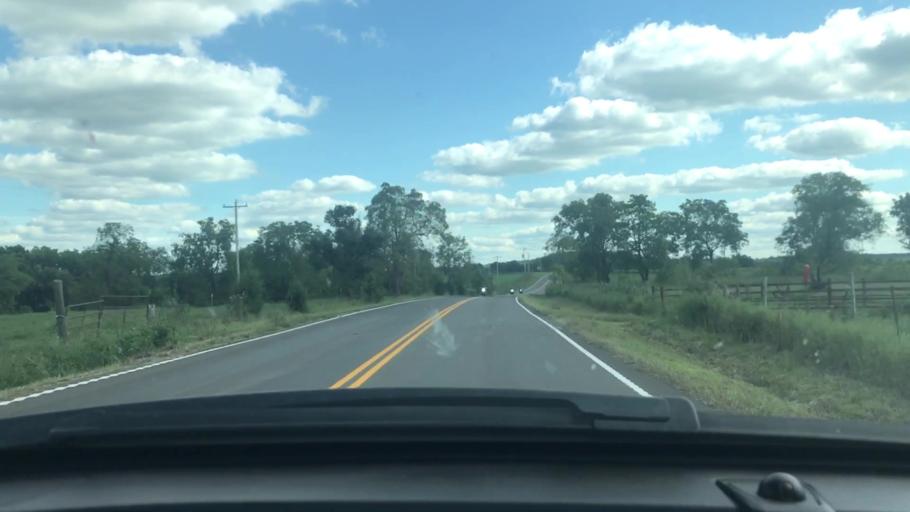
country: US
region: Missouri
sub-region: Wright County
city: Mountain Grove
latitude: 37.2947
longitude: -92.3086
